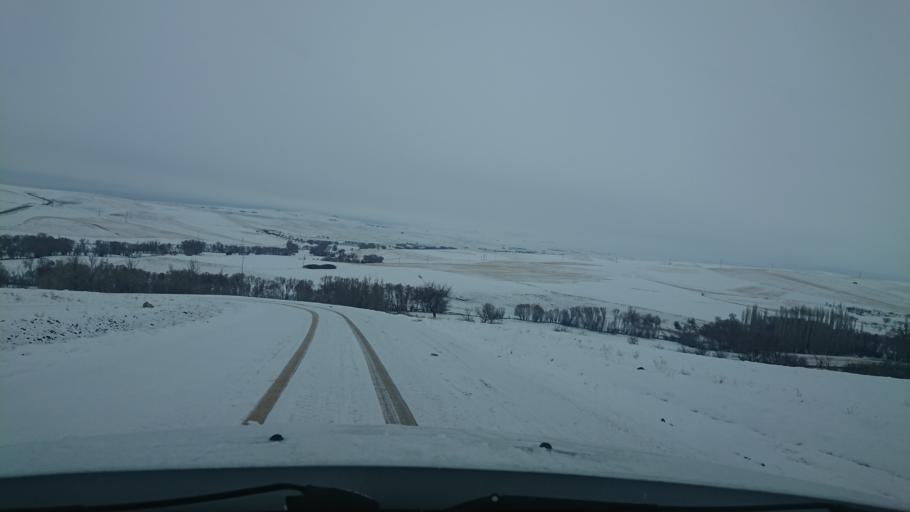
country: TR
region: Aksaray
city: Agacoren
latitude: 38.7548
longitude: 33.8762
